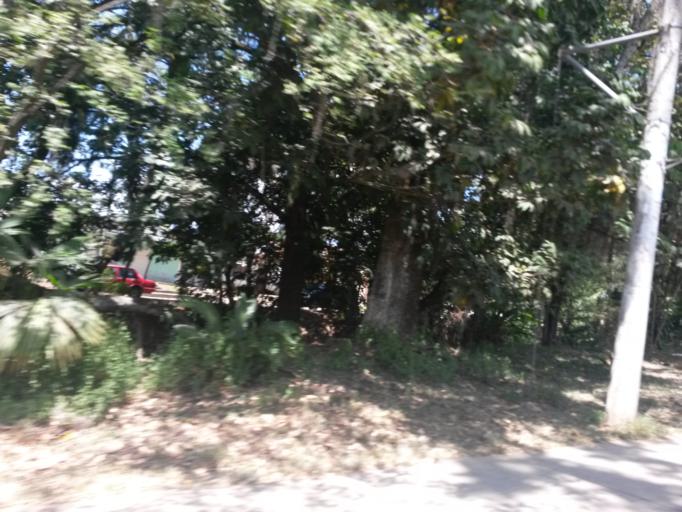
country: CO
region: Cauca
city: Santander de Quilichao
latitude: 3.0075
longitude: -76.4809
